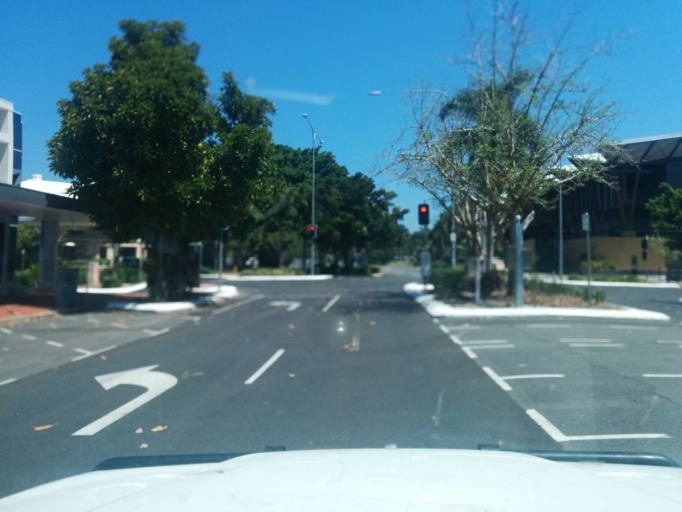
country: AU
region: Queensland
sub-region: Cairns
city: Cairns
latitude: -16.9262
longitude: 145.7776
